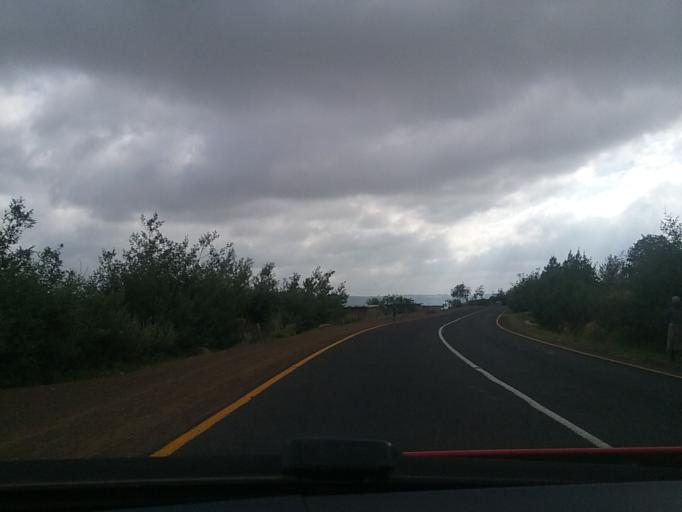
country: LS
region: Berea
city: Teyateyaneng
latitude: -29.1805
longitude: 27.7954
